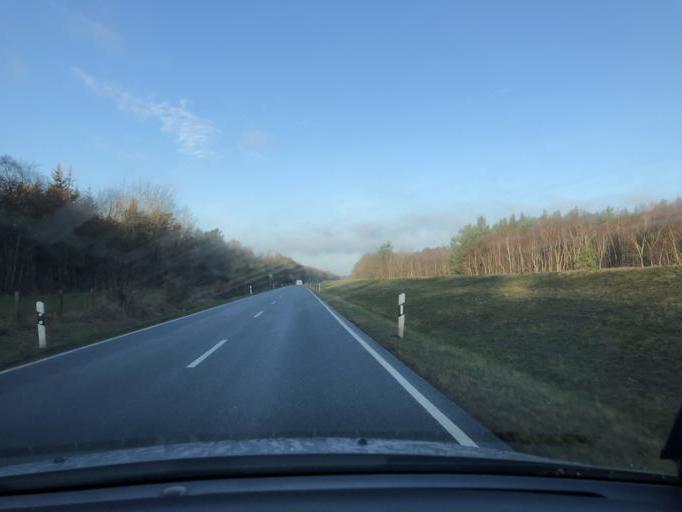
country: DE
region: Mecklenburg-Vorpommern
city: Zingst
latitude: 54.4436
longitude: 12.6385
